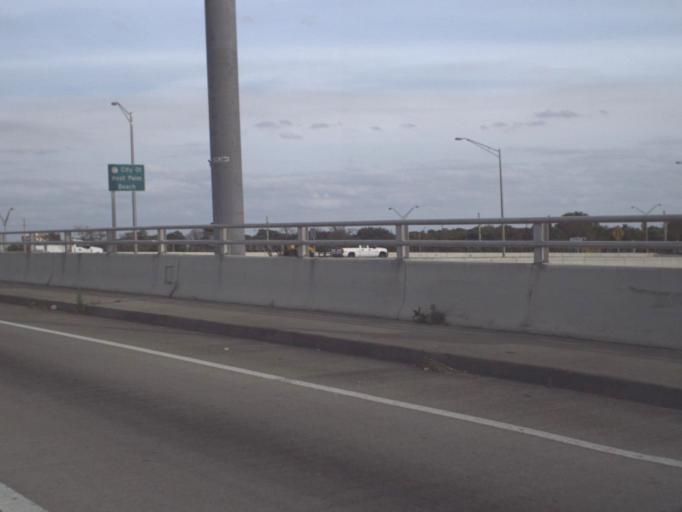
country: US
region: Florida
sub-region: Palm Beach County
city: Lake Clarke Shores
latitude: 26.6760
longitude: -80.0709
